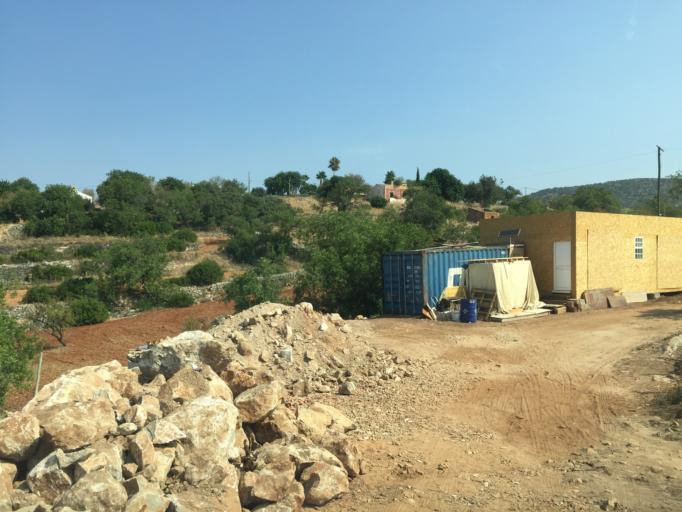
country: PT
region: Faro
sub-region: Loule
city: Almancil
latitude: 37.1018
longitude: -8.0110
